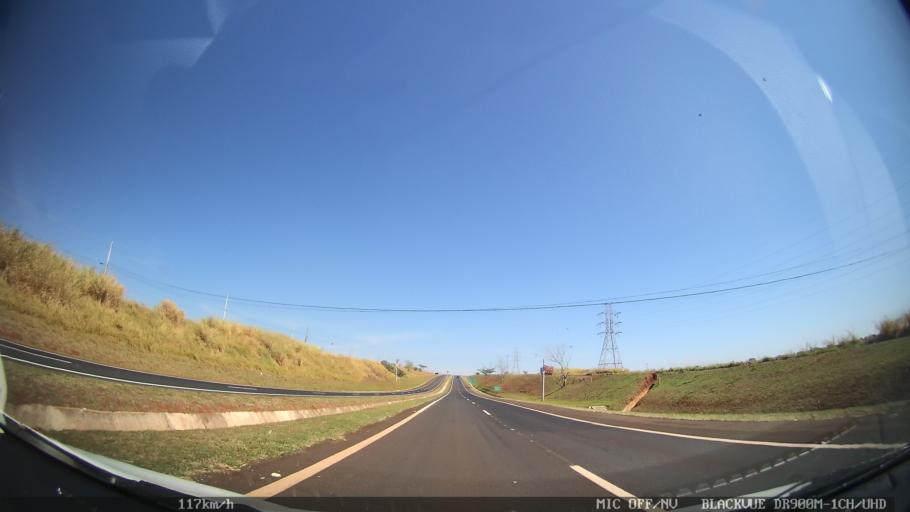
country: BR
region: Sao Paulo
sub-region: Ribeirao Preto
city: Ribeirao Preto
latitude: -21.1413
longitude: -47.8694
